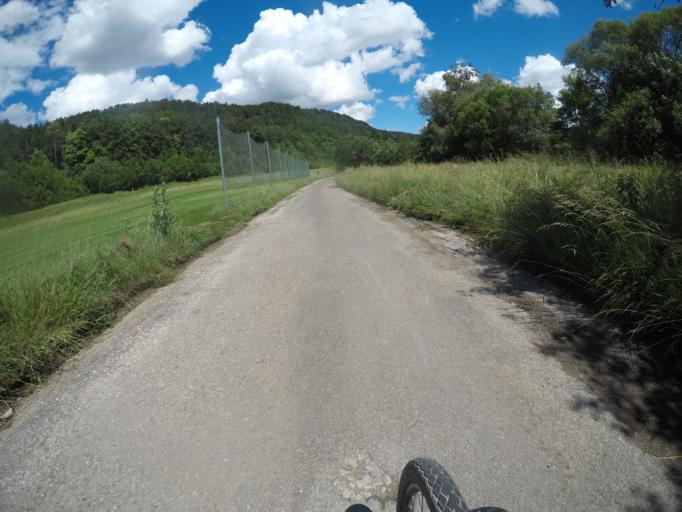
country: DE
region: Baden-Wuerttemberg
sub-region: Tuebingen Region
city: Hirrlingen
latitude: 48.4454
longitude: 8.8462
